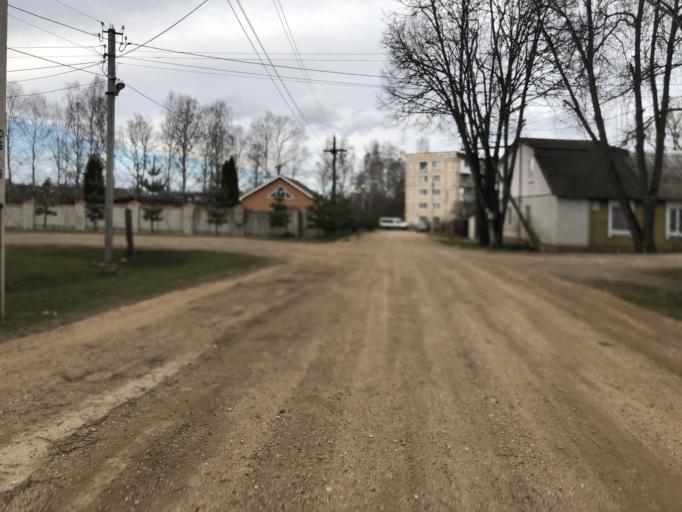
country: RU
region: Tverskaya
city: Rzhev
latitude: 56.2552
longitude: 34.3176
